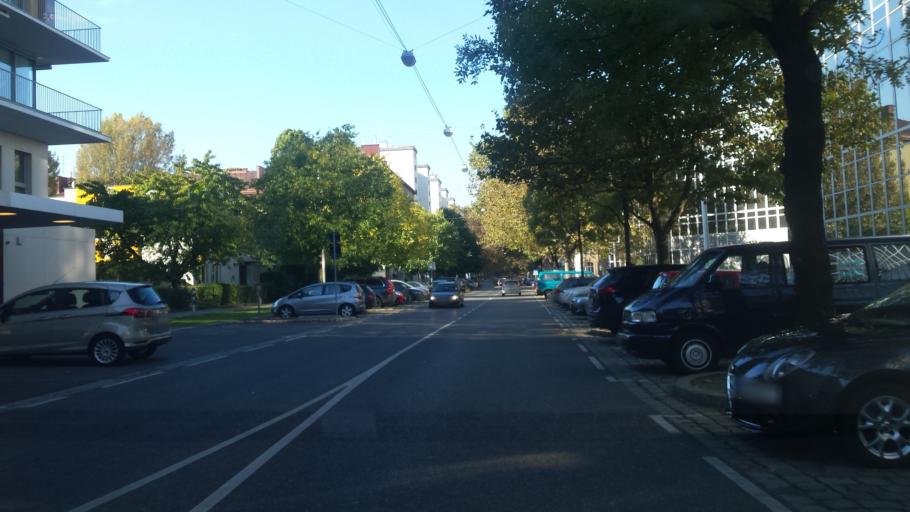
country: AT
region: Vienna
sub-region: Wien Stadt
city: Vienna
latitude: 48.2294
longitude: 16.3975
